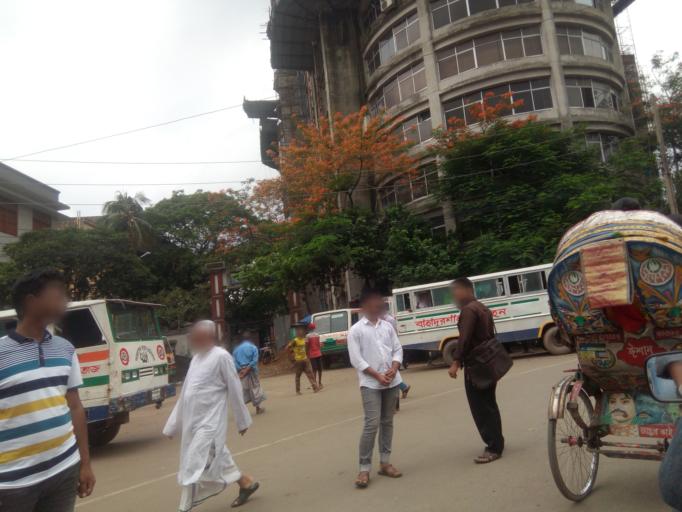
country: BD
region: Dhaka
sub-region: Dhaka
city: Dhaka
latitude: 23.7079
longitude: 90.4110
